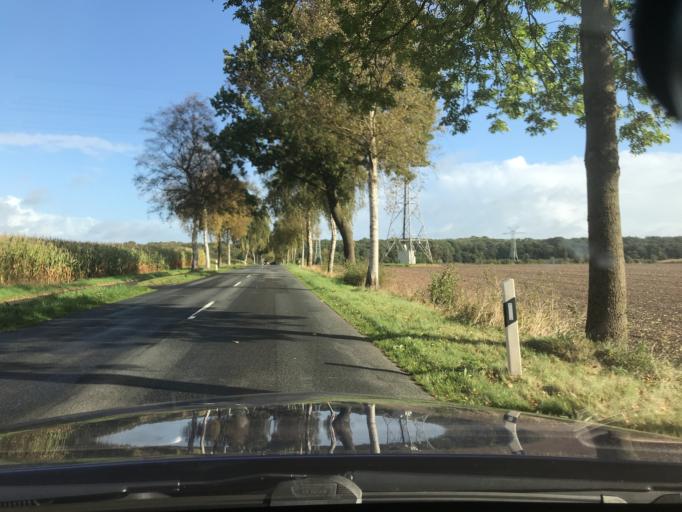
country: DE
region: Lower Saxony
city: Ahlerstedt
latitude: 53.4133
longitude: 9.4586
